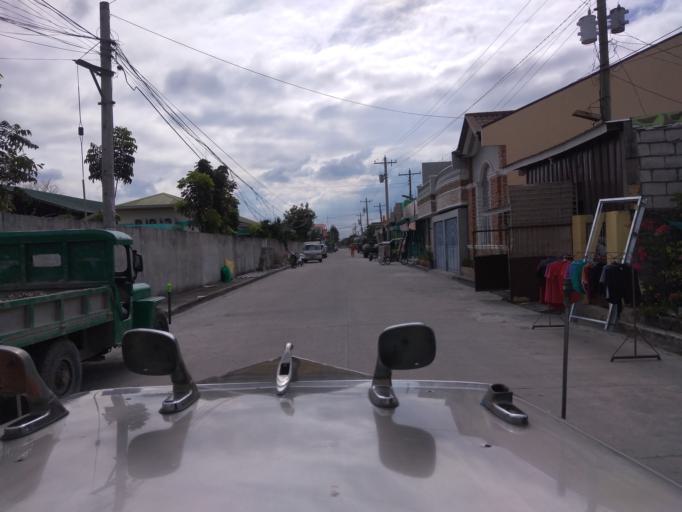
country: PH
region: Central Luzon
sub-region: Province of Pampanga
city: Pandacaqui
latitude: 15.1786
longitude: 120.6442
